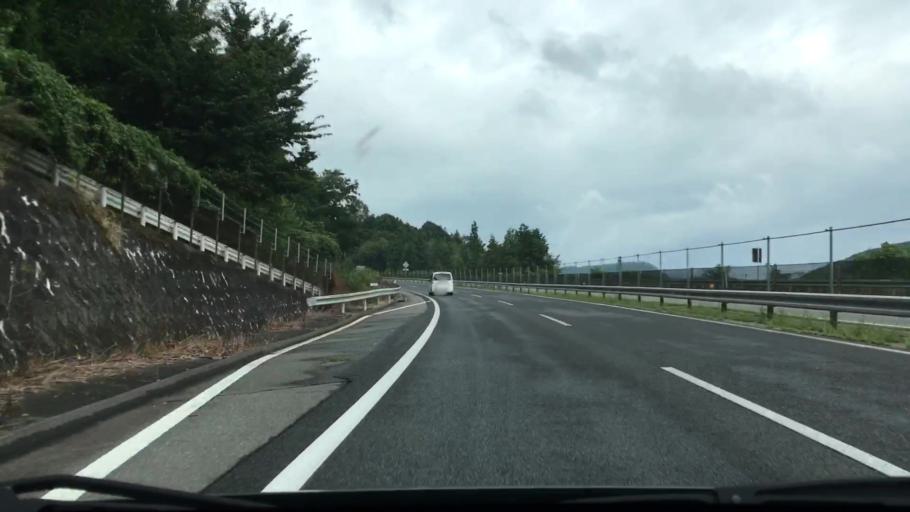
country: JP
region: Hiroshima
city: Miyoshi
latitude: 34.7192
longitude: 132.6531
